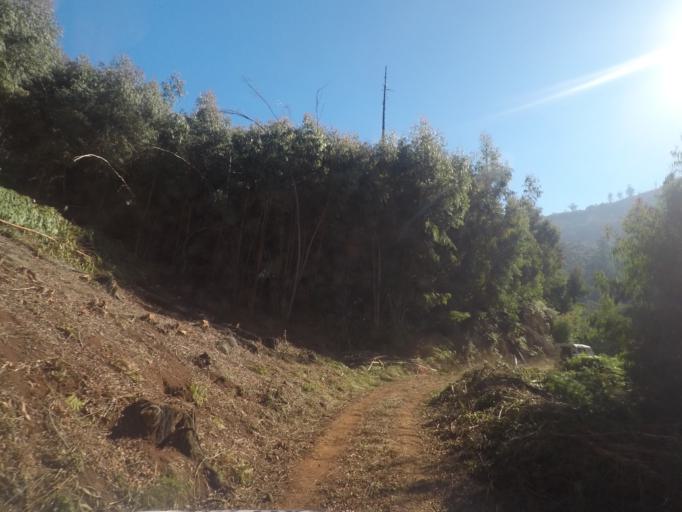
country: PT
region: Madeira
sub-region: Funchal
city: Nossa Senhora do Monte
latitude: 32.6919
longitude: -16.9121
